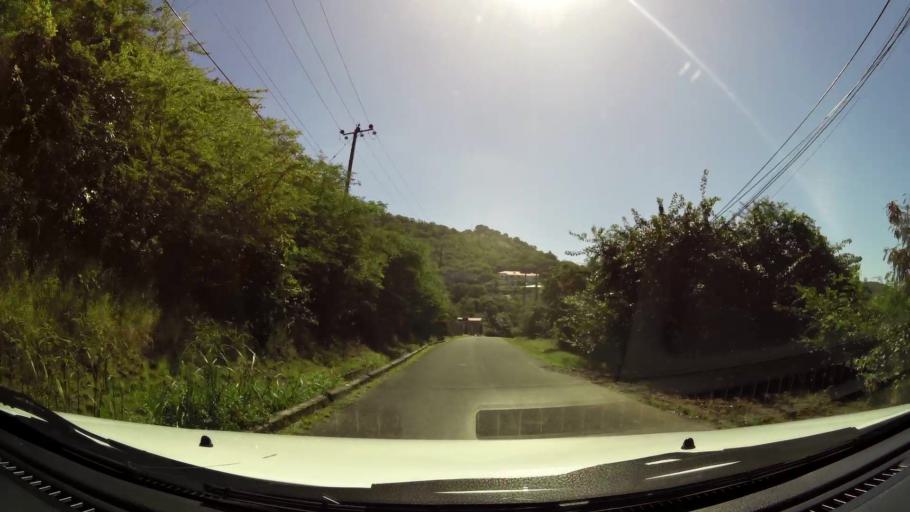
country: LC
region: Vieux-Fort
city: Vieux Fort
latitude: 13.7219
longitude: -60.9502
